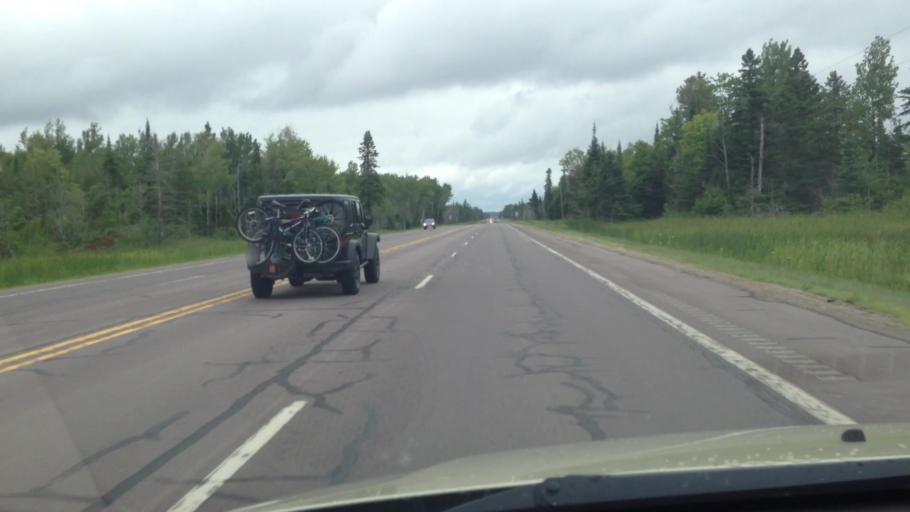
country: US
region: Michigan
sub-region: Schoolcraft County
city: Manistique
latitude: 46.0150
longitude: -85.9918
